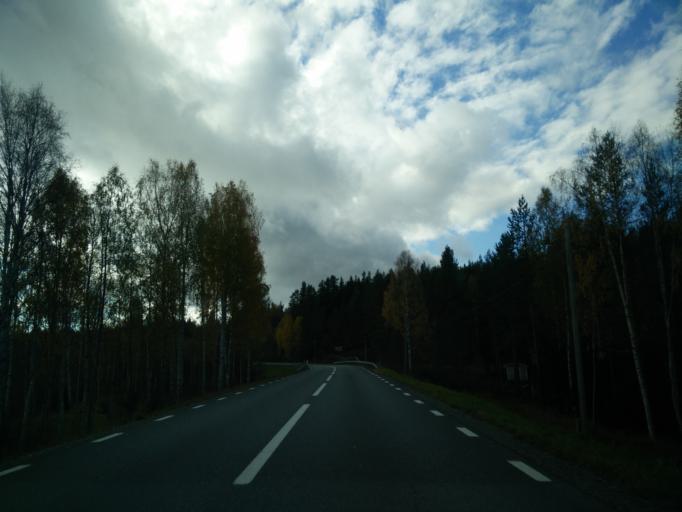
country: SE
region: Jaemtland
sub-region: Braecke Kommun
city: Braecke
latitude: 62.4545
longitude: 14.9557
